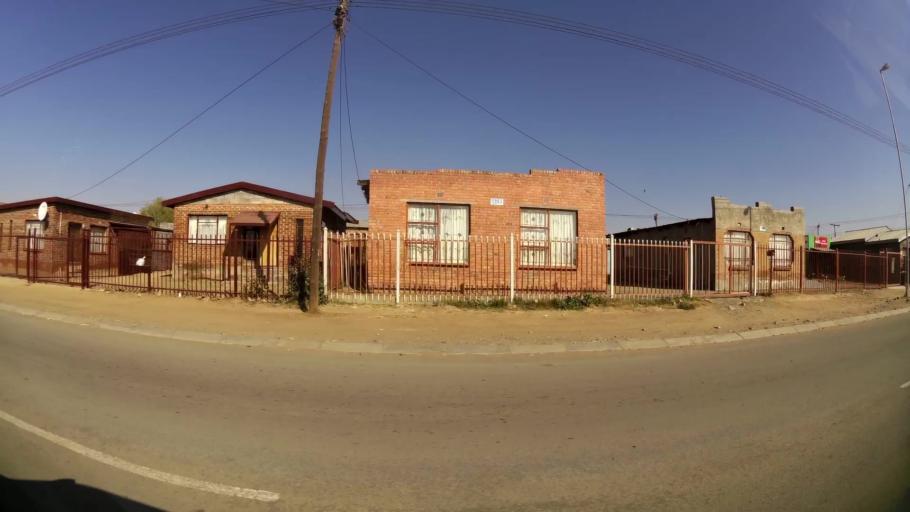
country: ZA
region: Orange Free State
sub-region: Mangaung Metropolitan Municipality
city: Bloemfontein
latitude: -29.1869
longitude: 26.2456
